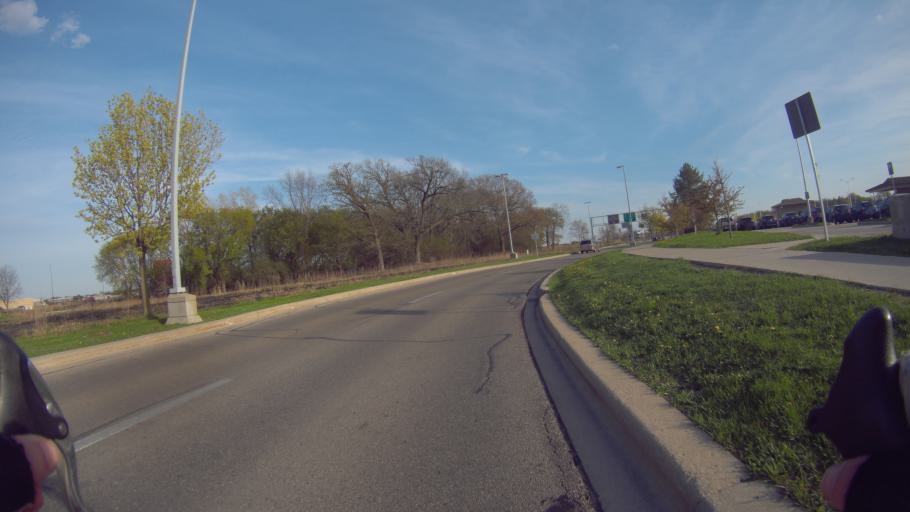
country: US
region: Wisconsin
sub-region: Dane County
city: Maple Bluff
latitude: 43.1334
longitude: -89.3485
